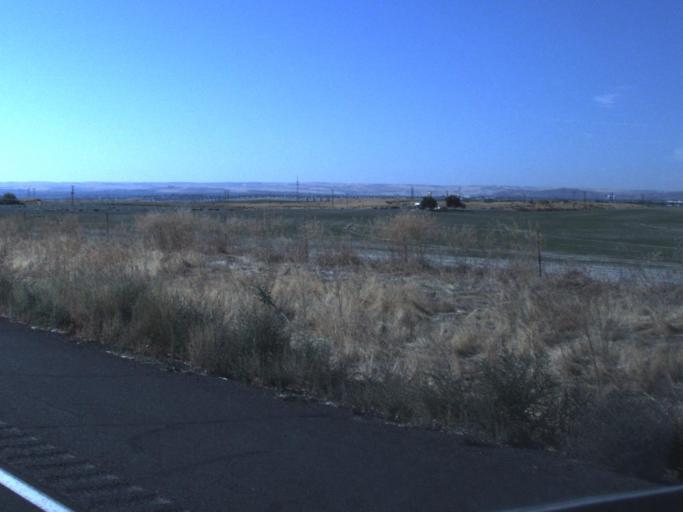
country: US
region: Washington
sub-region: Franklin County
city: Pasco
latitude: 46.3247
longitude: -119.0932
